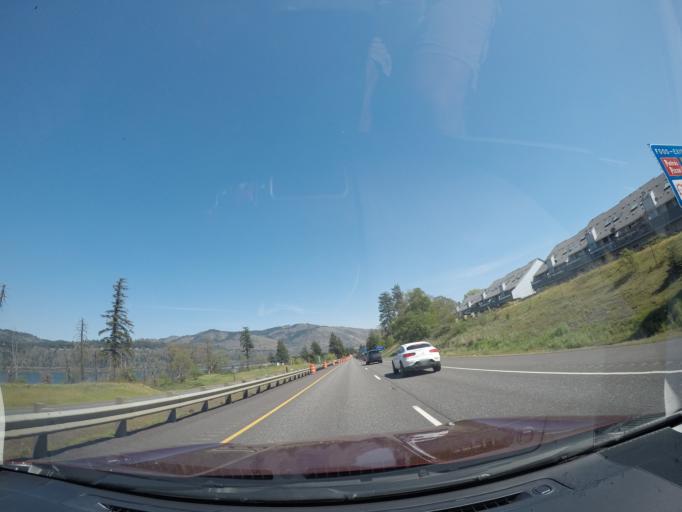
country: US
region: Oregon
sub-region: Hood River County
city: Hood River
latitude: 45.7128
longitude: -121.5271
